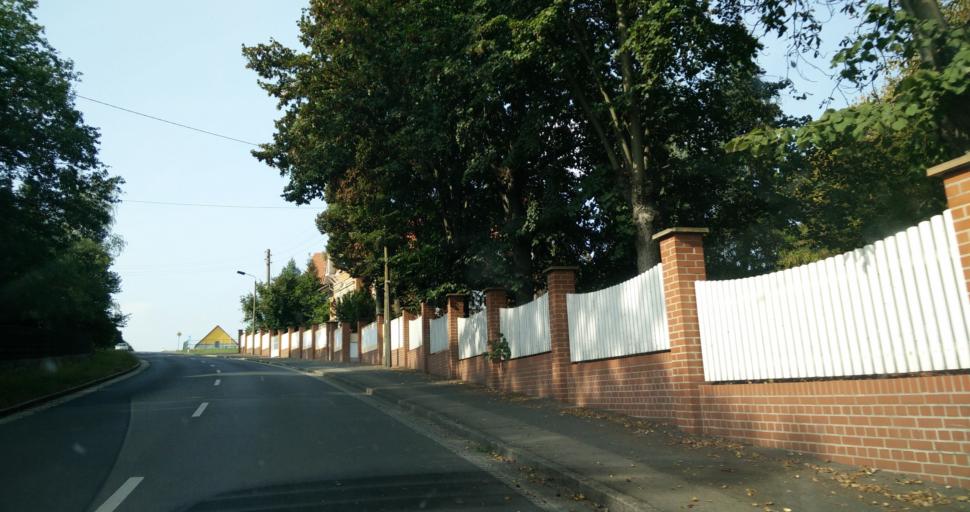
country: DE
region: Saxony
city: Colditz
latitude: 51.1353
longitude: 12.7968
